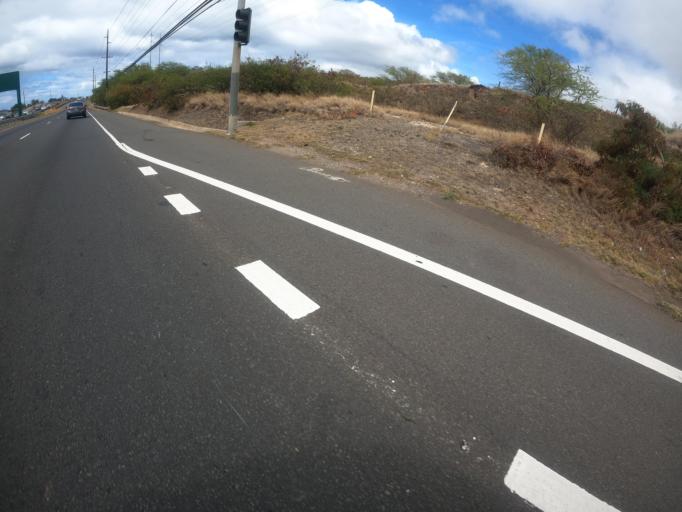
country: US
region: Hawaii
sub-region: Honolulu County
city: Makakilo City
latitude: 21.3418
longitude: -158.1070
